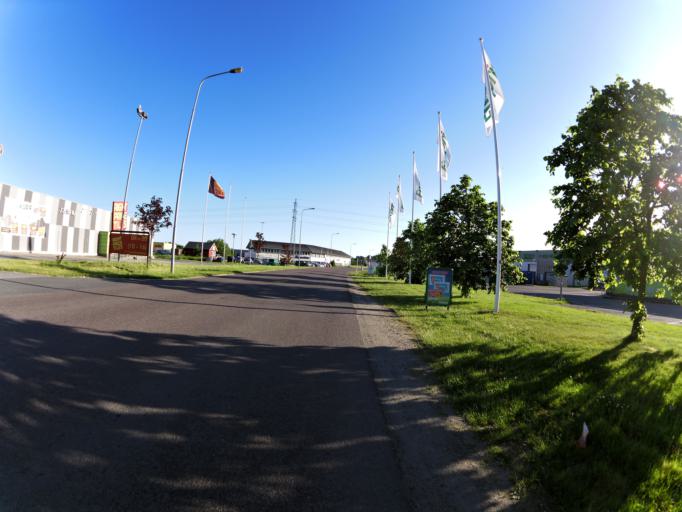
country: NO
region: Ostfold
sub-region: Fredrikstad
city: Fredrikstad
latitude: 59.2448
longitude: 10.9857
